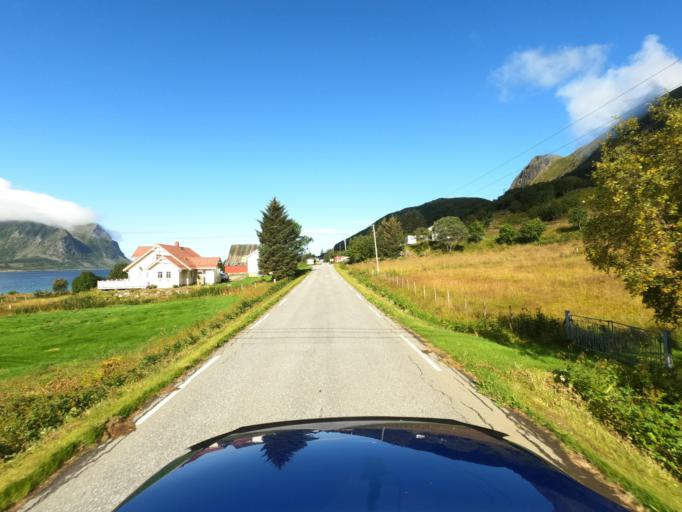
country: NO
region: Nordland
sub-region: Vagan
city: Kabelvag
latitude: 68.3000
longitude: 14.3191
